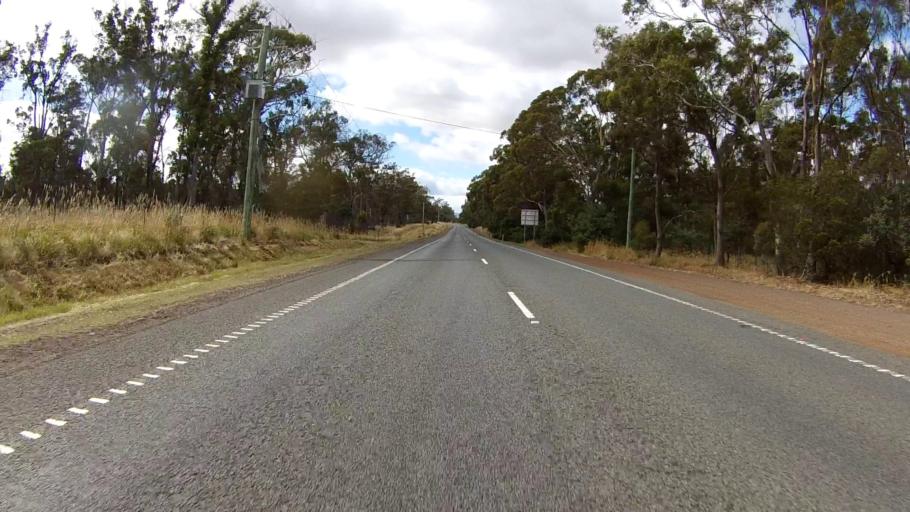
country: AU
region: Tasmania
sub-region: Northern Midlands
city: Evandale
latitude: -41.8222
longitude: 147.4264
